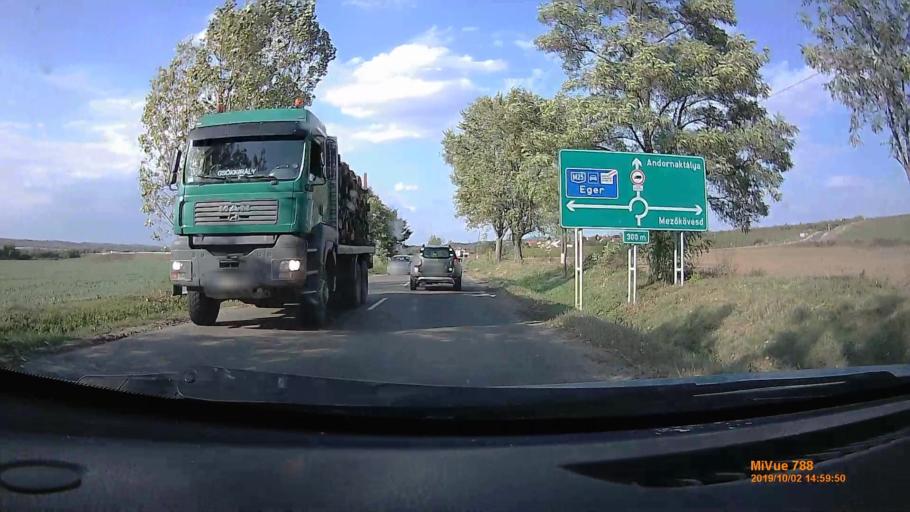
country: HU
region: Heves
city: Andornaktalya
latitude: 47.8286
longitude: 20.4191
